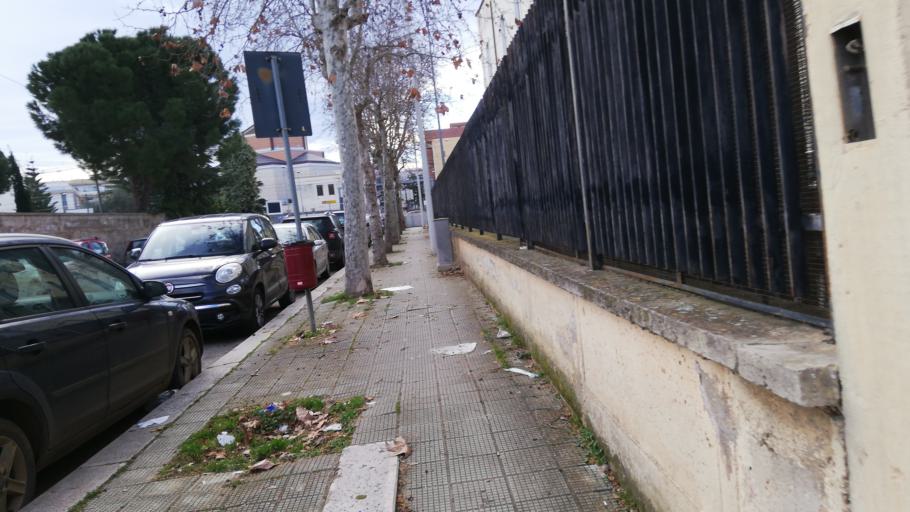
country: IT
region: Apulia
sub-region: Provincia di Bari
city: Bitonto
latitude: 41.1161
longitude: 16.6901
